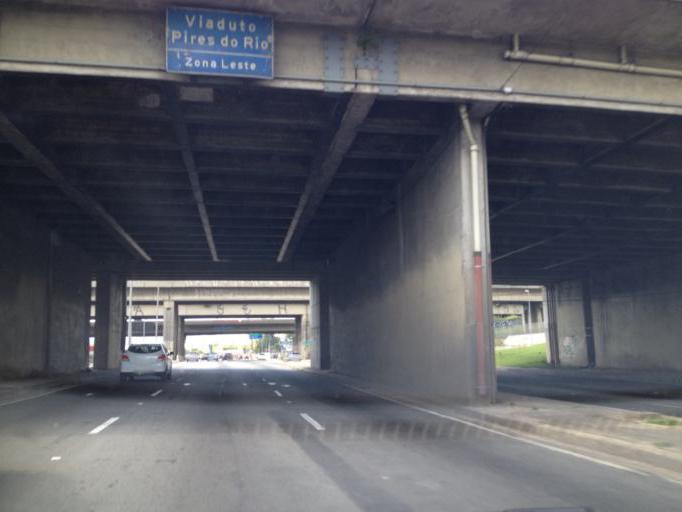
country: BR
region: Sao Paulo
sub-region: Sao Paulo
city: Sao Paulo
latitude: -23.5422
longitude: -46.5805
